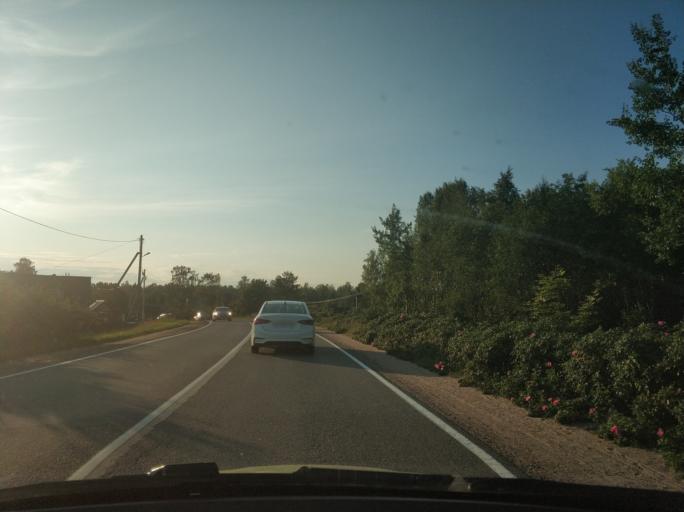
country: RU
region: Leningrad
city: Borisova Griva
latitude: 60.0904
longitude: 31.0181
